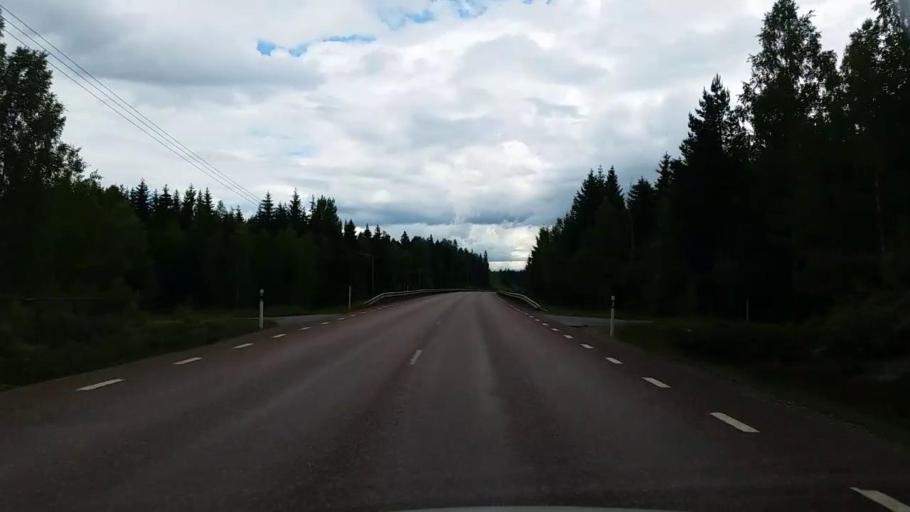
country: SE
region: Gaevleborg
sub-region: Hofors Kommun
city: Hofors
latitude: 60.5067
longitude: 16.4327
